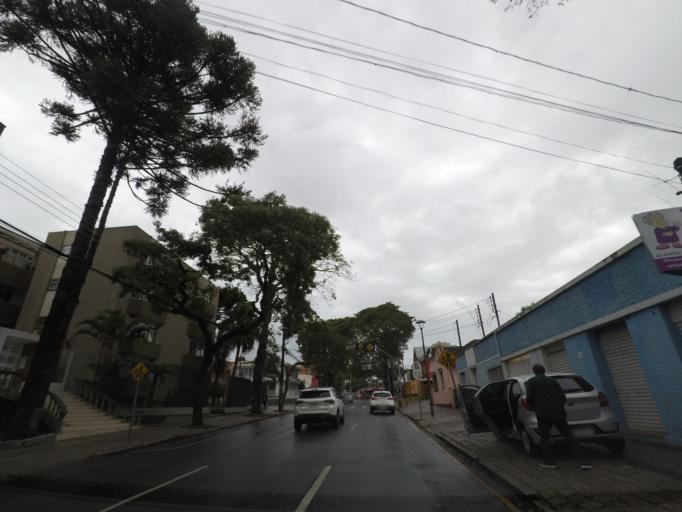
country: BR
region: Parana
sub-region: Curitiba
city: Curitiba
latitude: -25.4518
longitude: -49.2785
